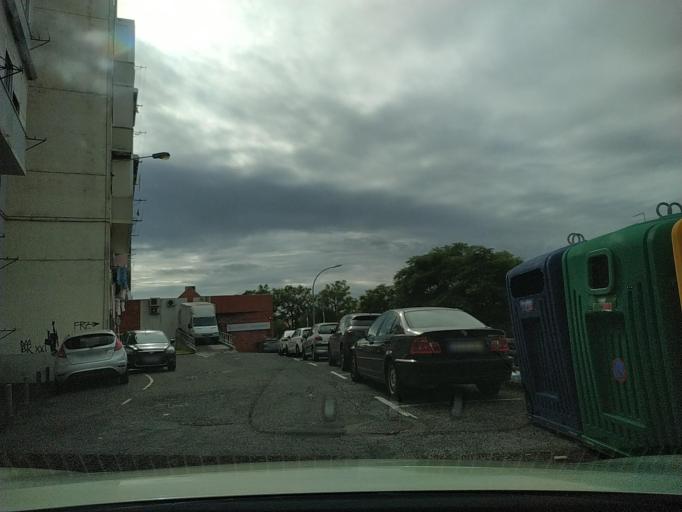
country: PT
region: Lisbon
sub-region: Amadora
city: Amadora
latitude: 38.7569
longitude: -9.2424
